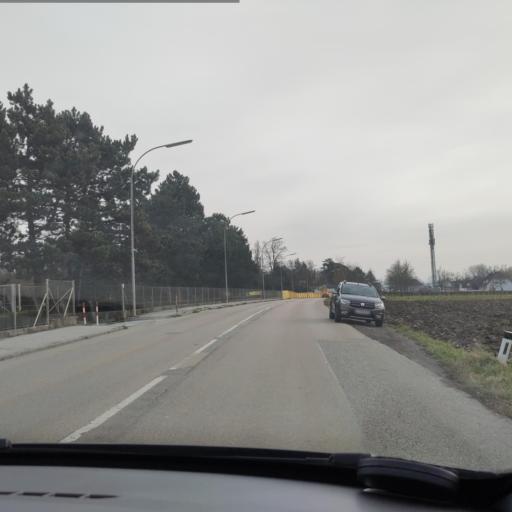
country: AT
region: Lower Austria
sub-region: Sankt Polten Stadt
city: Sankt Poelten
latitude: 48.2160
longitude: 15.6084
